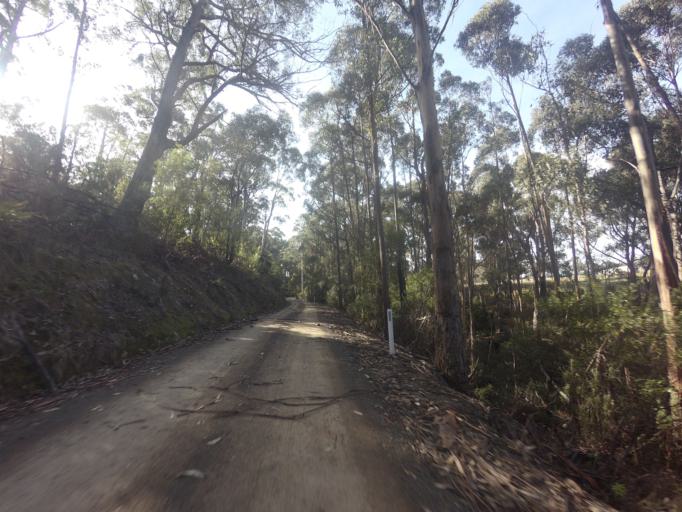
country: AU
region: Tasmania
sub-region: Kingborough
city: Kettering
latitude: -43.1016
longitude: 147.2606
